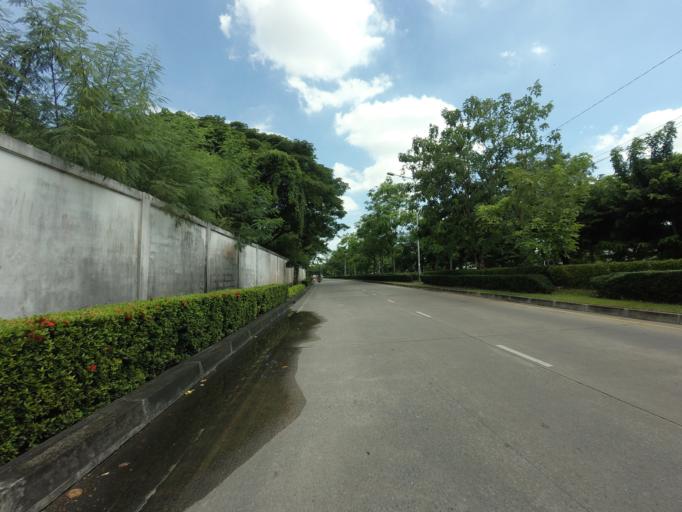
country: TH
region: Bangkok
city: Chatuchak
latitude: 13.8472
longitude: 100.5890
